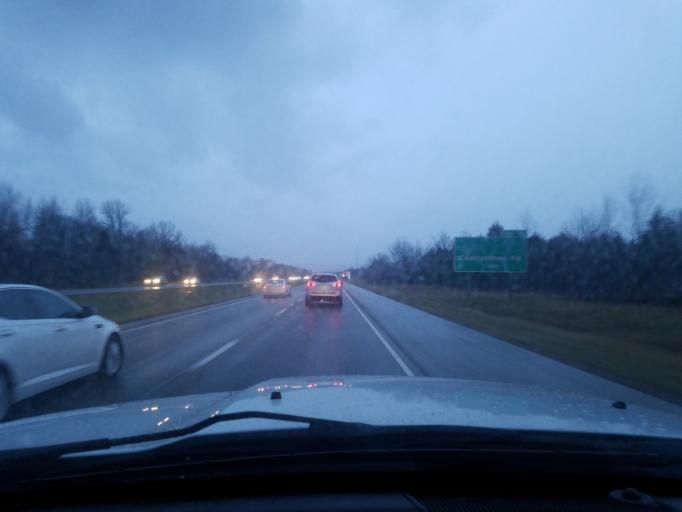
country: US
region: Indiana
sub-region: Clark County
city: Clarksville
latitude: 38.3454
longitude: -85.7728
